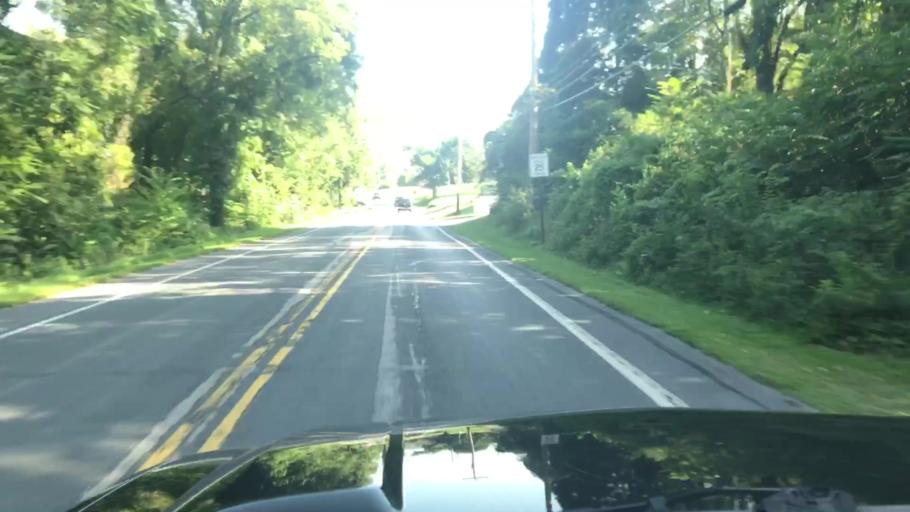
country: US
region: Pennsylvania
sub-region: York County
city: Valley Green
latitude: 40.1623
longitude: -76.8173
